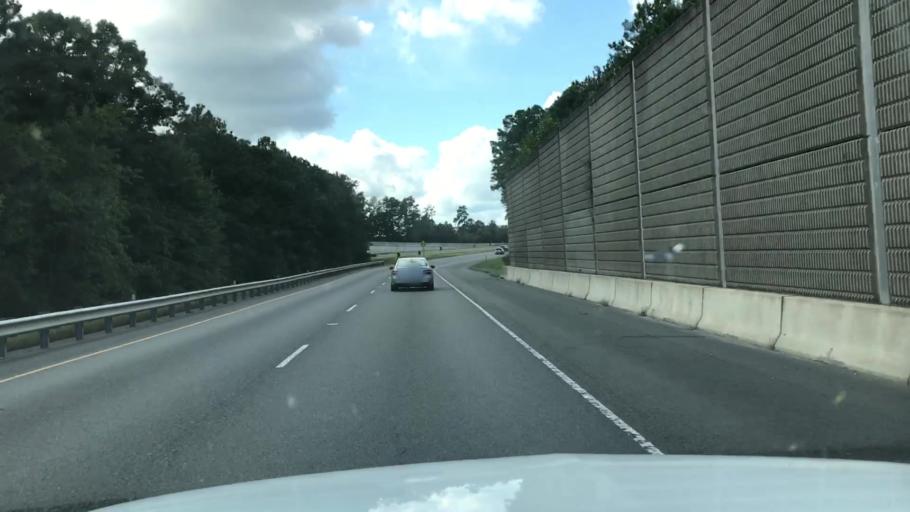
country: US
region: Virginia
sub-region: Henrico County
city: Short Pump
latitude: 37.6575
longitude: -77.6060
